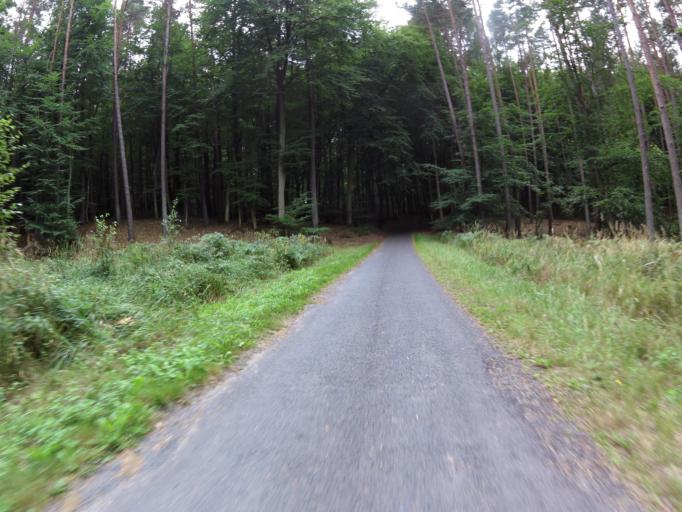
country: DE
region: Mecklenburg-Vorpommern
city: Seebad Heringsdorf
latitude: 53.9262
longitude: 14.1718
